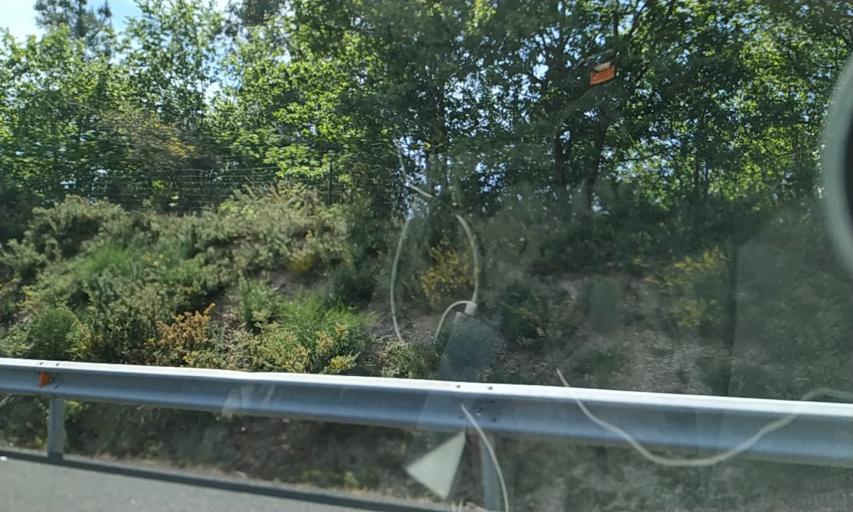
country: ES
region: Galicia
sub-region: Provincia de Pontevedra
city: Portas
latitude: 42.5457
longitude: -8.6691
